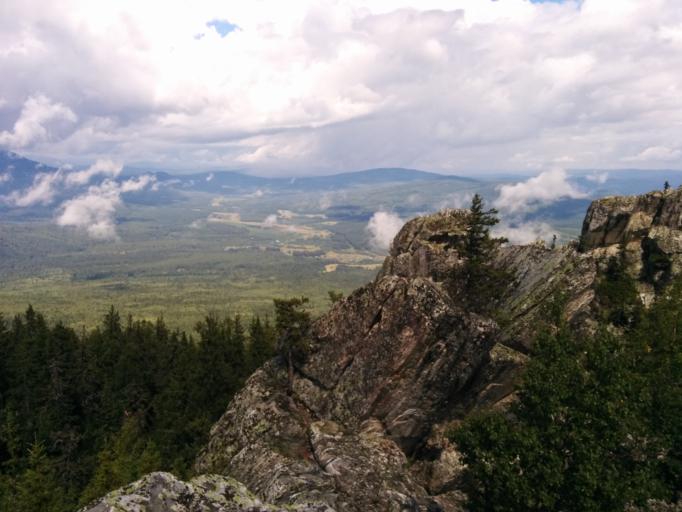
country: RU
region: Bashkortostan
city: Beloretsk
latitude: 54.0207
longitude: 58.2915
